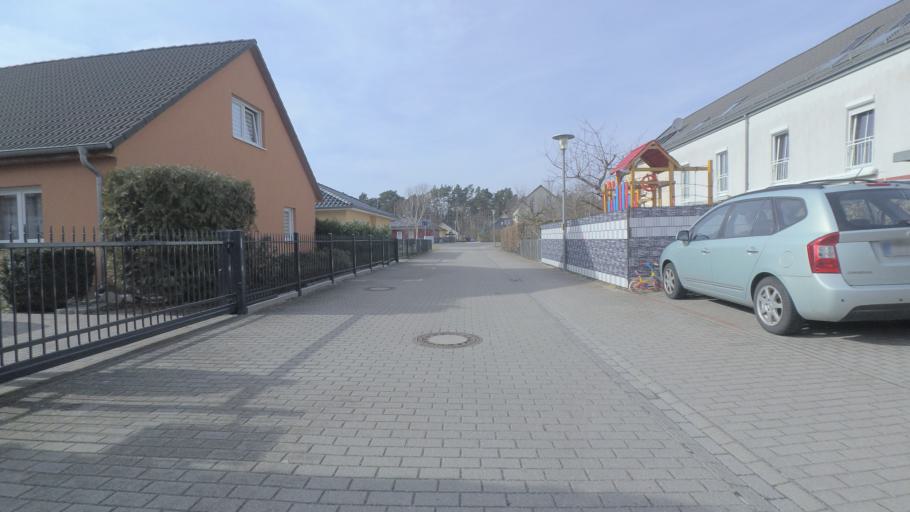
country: DE
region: Brandenburg
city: Ludwigsfelde
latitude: 52.3118
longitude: 13.2297
